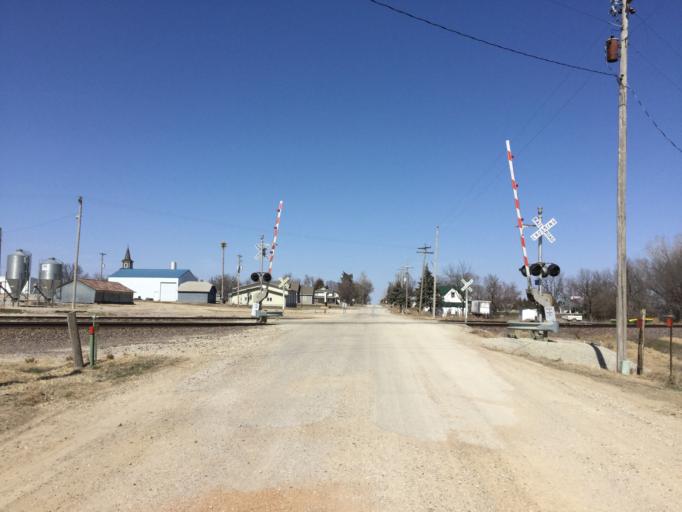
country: US
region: Kansas
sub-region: Marshall County
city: Marysville
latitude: 39.8399
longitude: -96.5201
